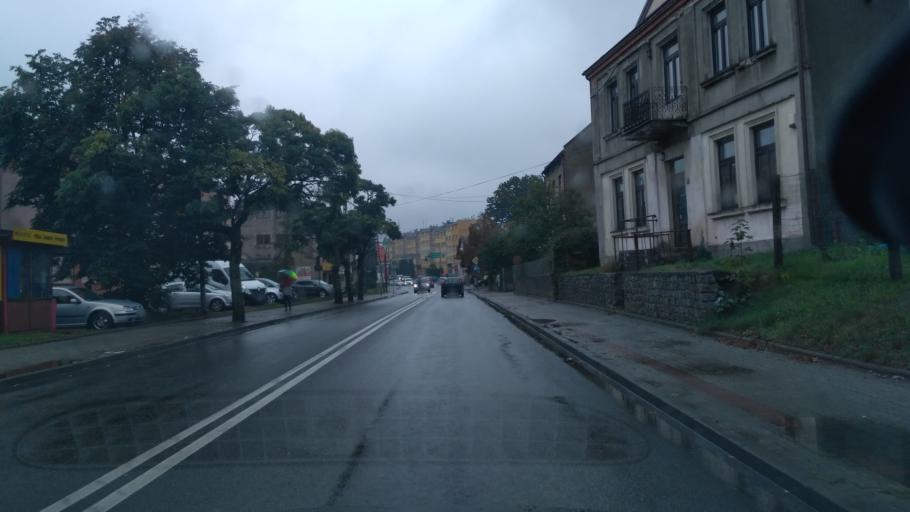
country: PL
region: Subcarpathian Voivodeship
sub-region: Powiat debicki
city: Debica
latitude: 50.0530
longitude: 21.4108
